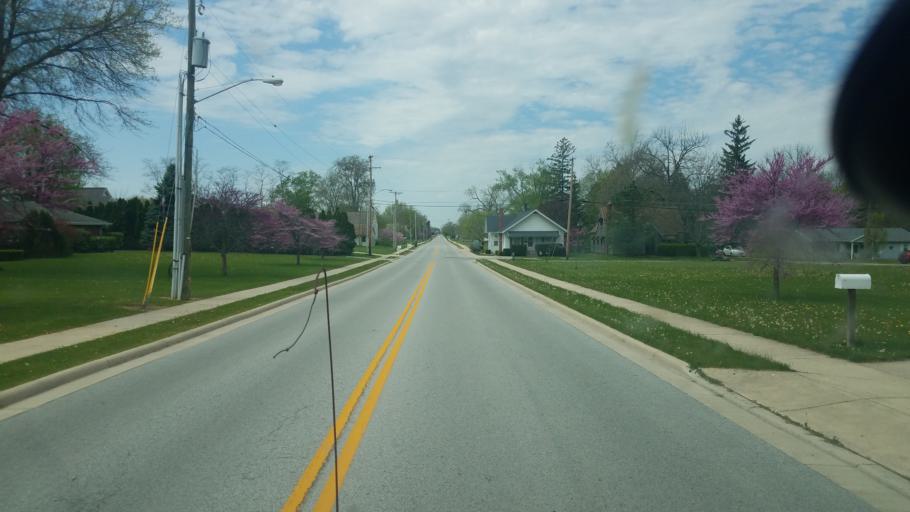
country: US
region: Ohio
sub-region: Hardin County
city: Ada
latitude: 40.7621
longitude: -83.8249
